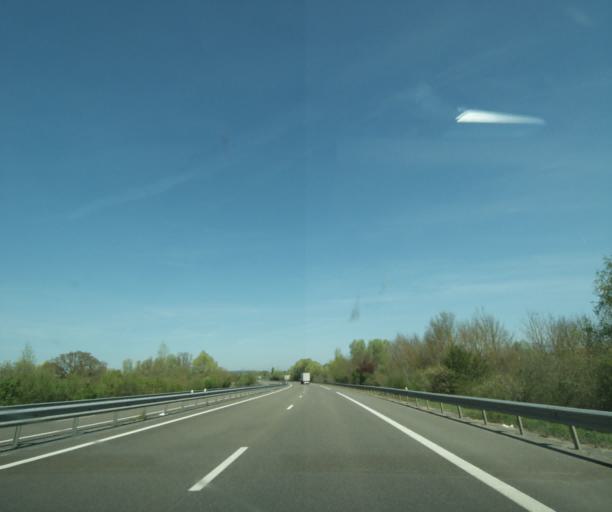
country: FR
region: Bourgogne
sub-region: Departement de la Nievre
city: Saint-Eloi
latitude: 46.9854
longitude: 3.2061
